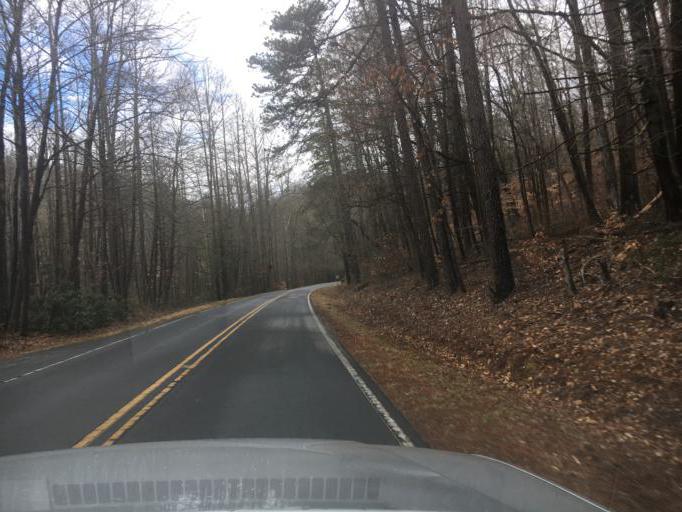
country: US
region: North Carolina
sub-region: Transylvania County
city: Brevard
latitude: 35.2861
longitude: -82.7436
